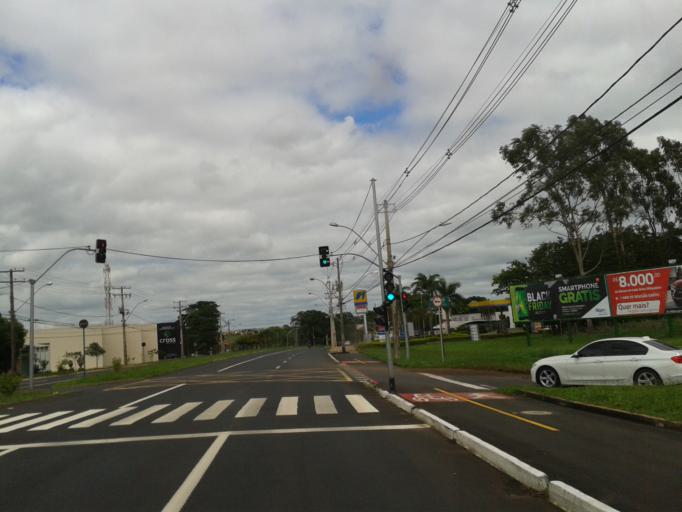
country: BR
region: Minas Gerais
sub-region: Uberaba
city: Uberaba
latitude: -19.7494
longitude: -47.9746
